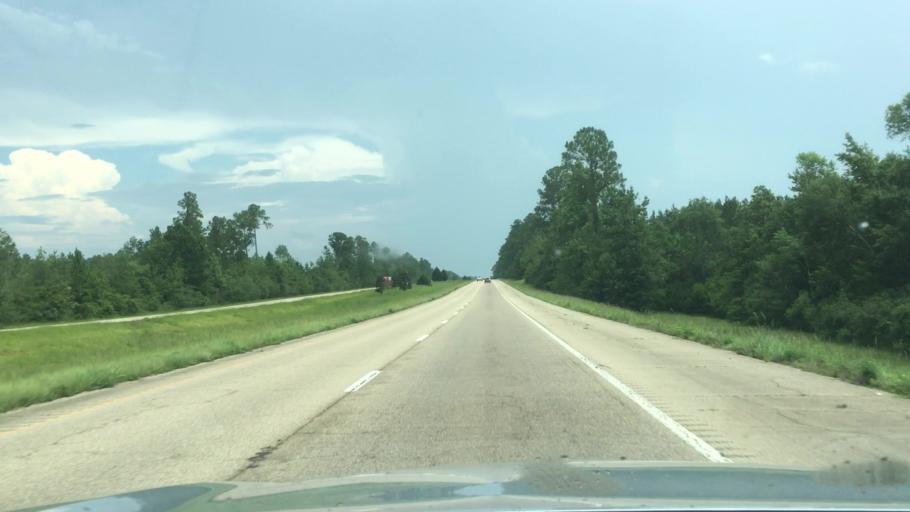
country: US
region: Mississippi
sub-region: Lamar County
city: Lumberton
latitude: 30.9707
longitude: -89.4338
